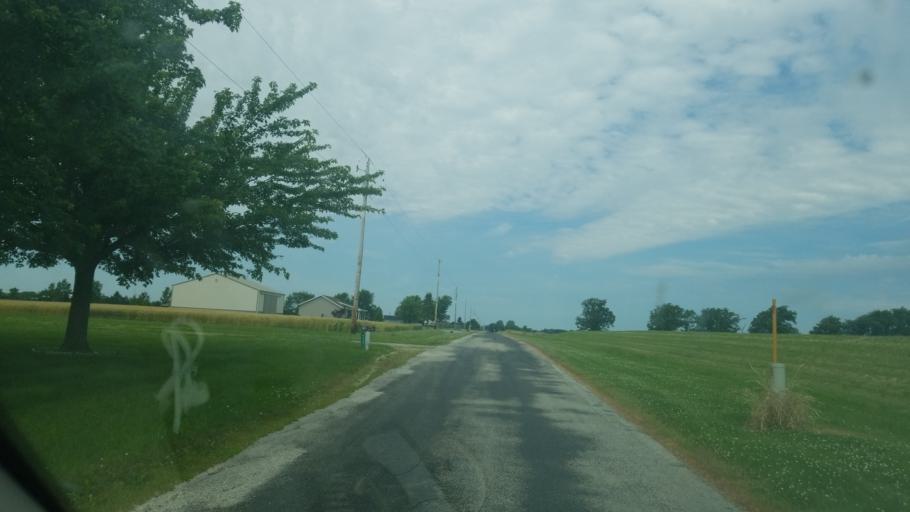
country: US
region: Ohio
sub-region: Wood County
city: North Baltimore
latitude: 41.2323
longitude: -83.5808
